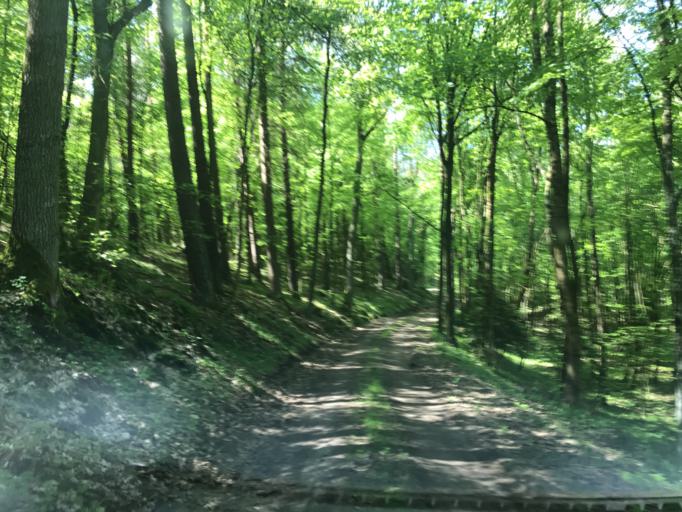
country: PL
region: Kujawsko-Pomorskie
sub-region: Powiat brodnicki
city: Gorzno
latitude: 53.2141
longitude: 19.7285
